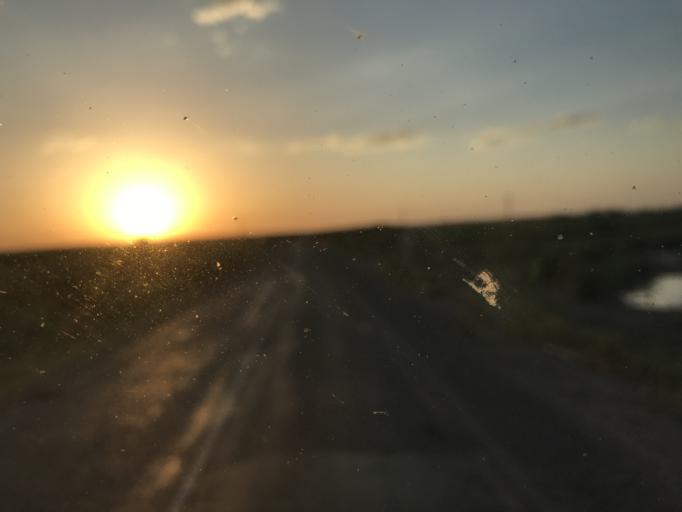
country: UZ
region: Toshkent
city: Yangiyul
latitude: 41.3812
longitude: 68.7764
